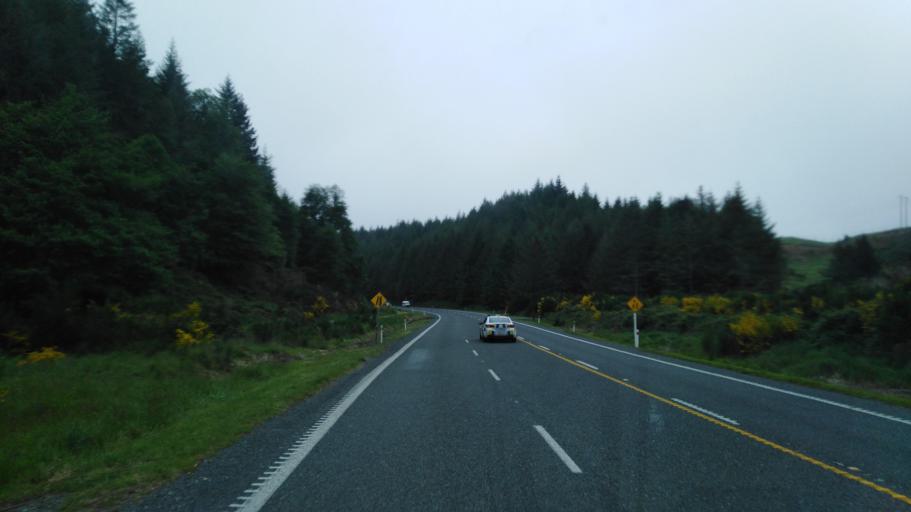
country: NZ
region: Bay of Plenty
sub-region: Rotorua District
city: Rotorua
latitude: -38.2368
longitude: 176.3007
